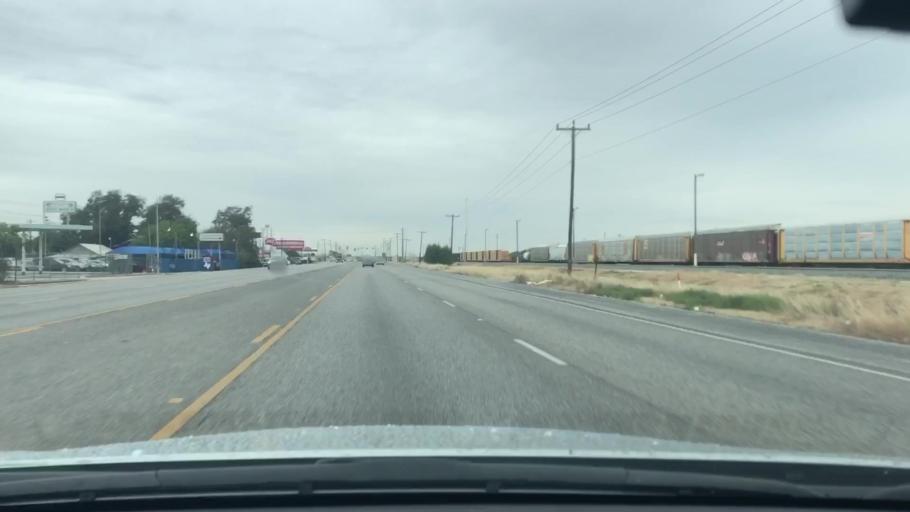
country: US
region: Texas
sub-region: Bexar County
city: Kirby
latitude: 29.4663
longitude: -98.3945
